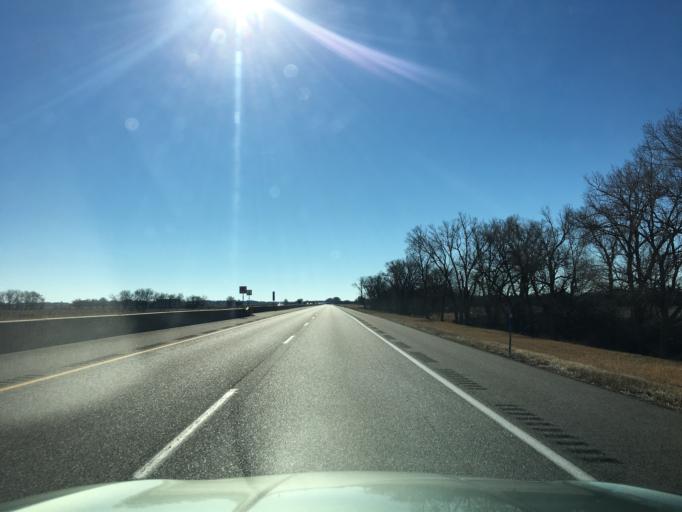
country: US
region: Kansas
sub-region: Sumner County
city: Belle Plaine
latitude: 37.4609
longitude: -97.3226
